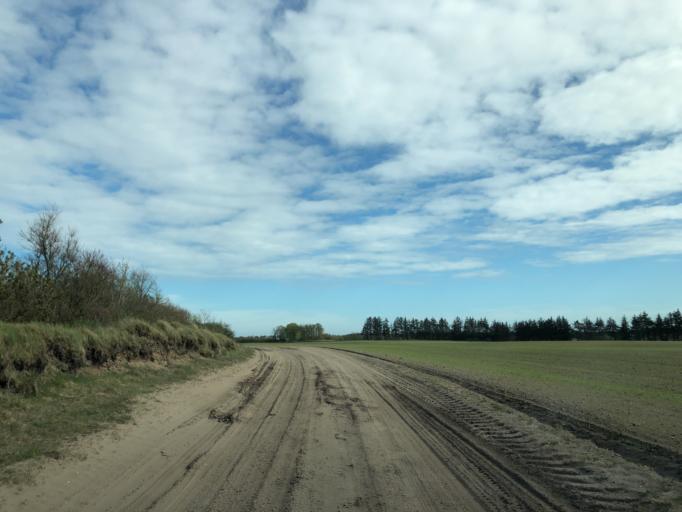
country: DK
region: Central Jutland
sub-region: Holstebro Kommune
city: Ulfborg
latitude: 56.2456
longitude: 8.3405
